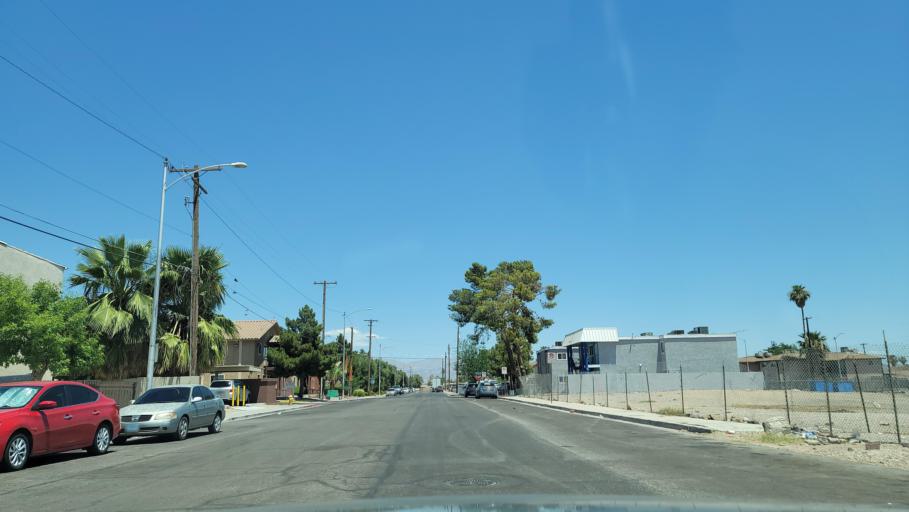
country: US
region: Nevada
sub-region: Clark County
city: North Las Vegas
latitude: 36.1857
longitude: -115.1183
